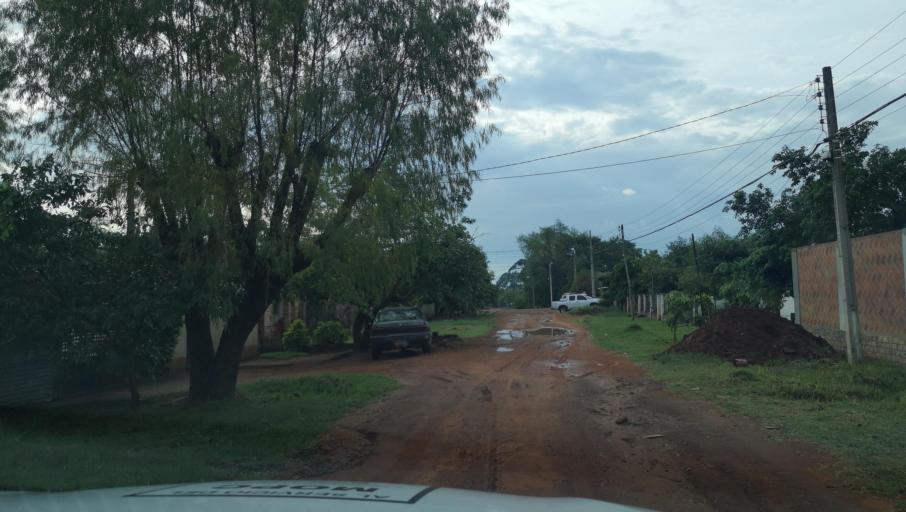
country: PY
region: Misiones
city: Santa Maria
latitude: -26.8818
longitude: -57.0229
